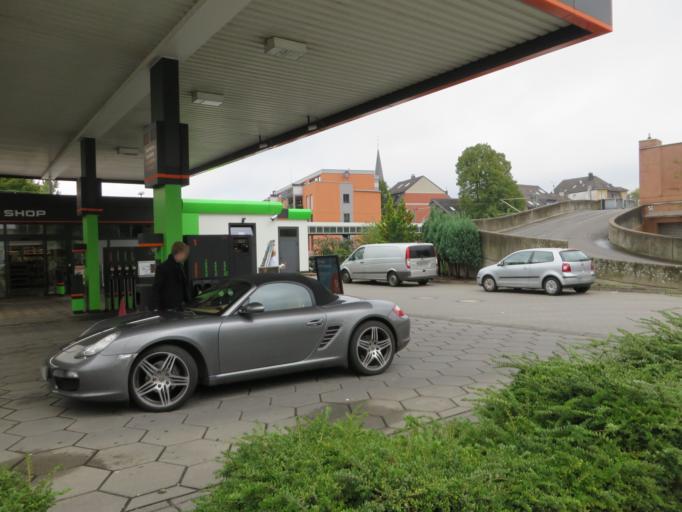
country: DE
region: North Rhine-Westphalia
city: Witten
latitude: 51.4476
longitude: 7.3753
